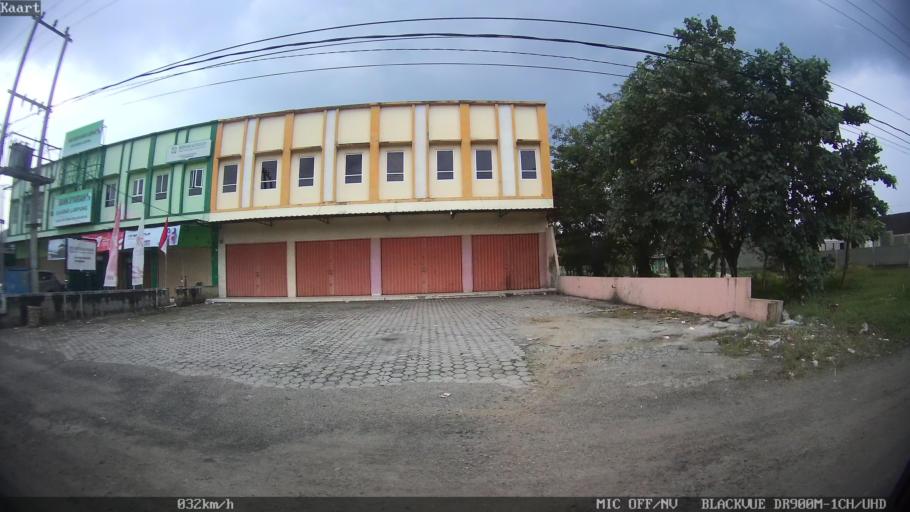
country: ID
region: Lampung
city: Gedongtataan
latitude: -5.3752
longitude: 105.0869
